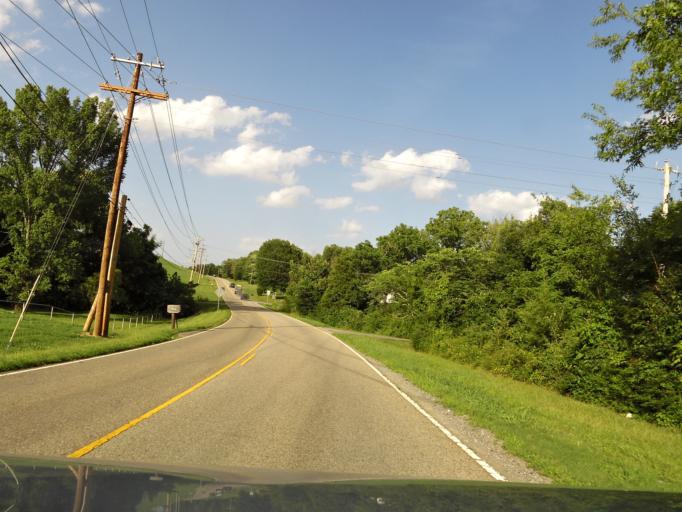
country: US
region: Tennessee
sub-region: Blount County
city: Eagleton Village
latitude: 35.8073
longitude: -83.9262
